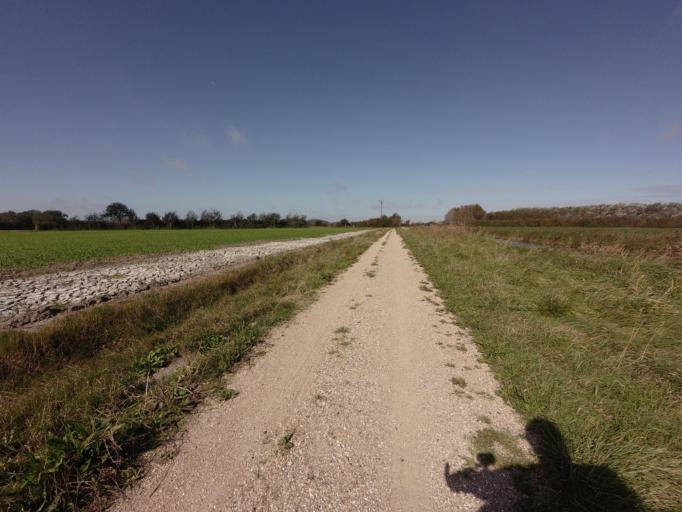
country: NL
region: Zeeland
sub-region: Gemeente Vlissingen
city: Vlissingen
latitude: 51.4856
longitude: 3.5319
